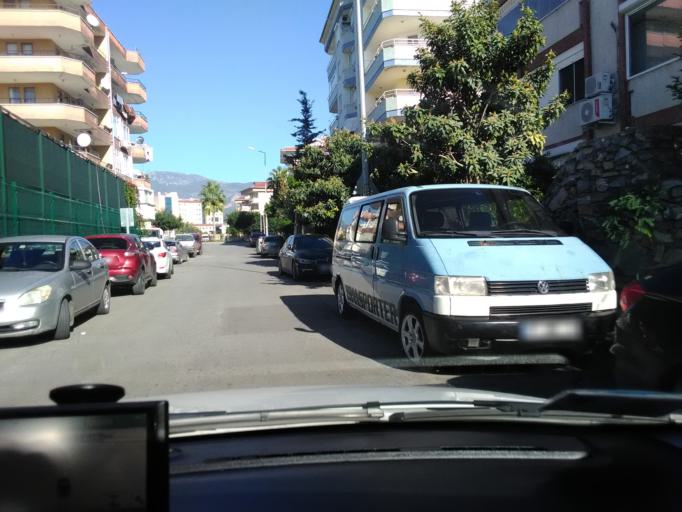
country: TR
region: Antalya
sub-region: Alanya
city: Alanya
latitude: 36.5365
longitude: 32.0418
